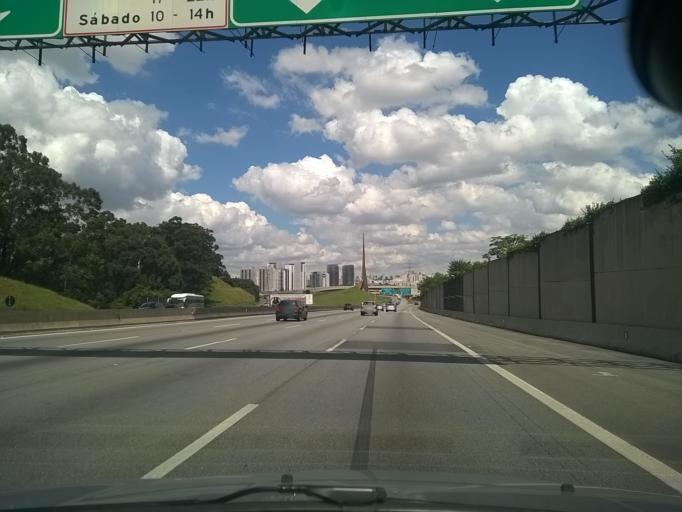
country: BR
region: Sao Paulo
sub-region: Osasco
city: Osasco
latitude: -23.5055
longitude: -46.7232
